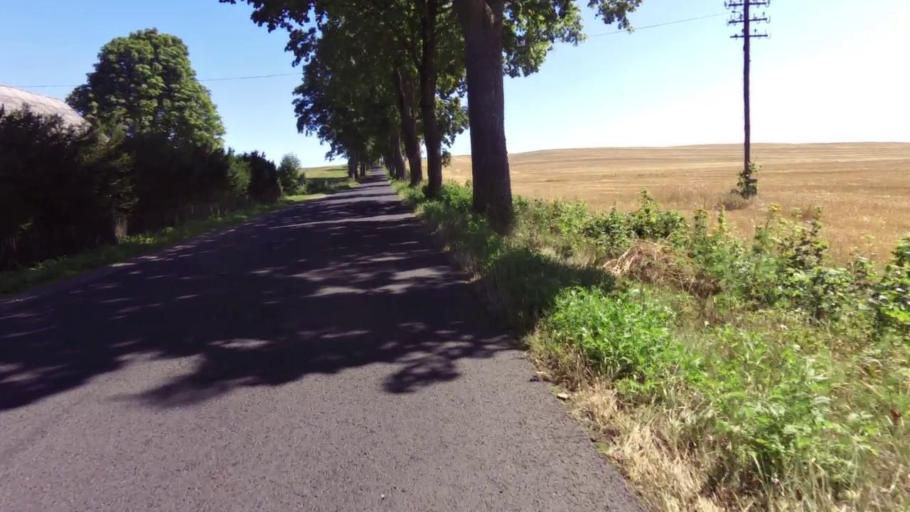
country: PL
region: West Pomeranian Voivodeship
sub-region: Powiat drawski
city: Czaplinek
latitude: 53.5605
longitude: 16.2826
